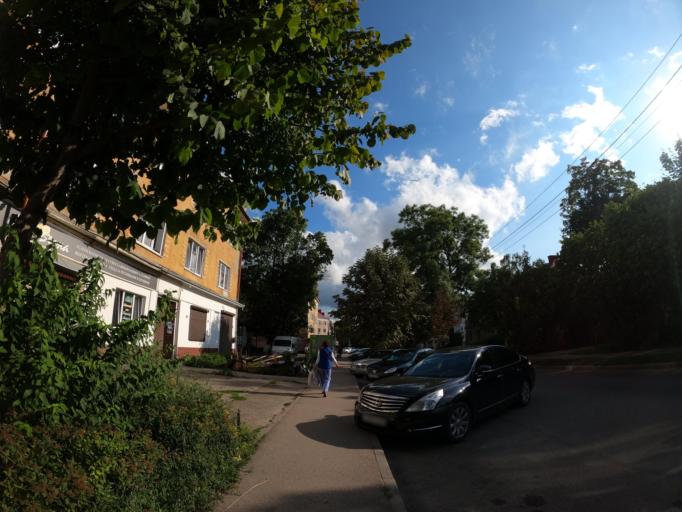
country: RU
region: Kaliningrad
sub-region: Gorod Kaliningrad
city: Kaliningrad
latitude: 54.7253
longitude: 20.4644
